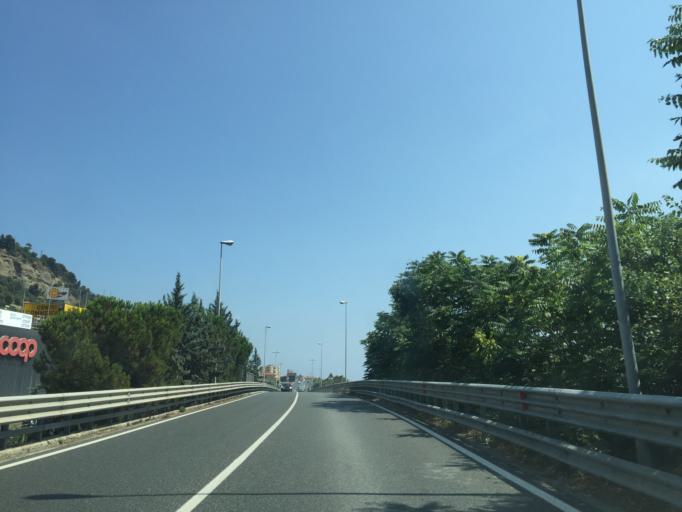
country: IT
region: Liguria
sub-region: Provincia di Imperia
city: Ventimiglia
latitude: 43.8007
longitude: 7.5981
